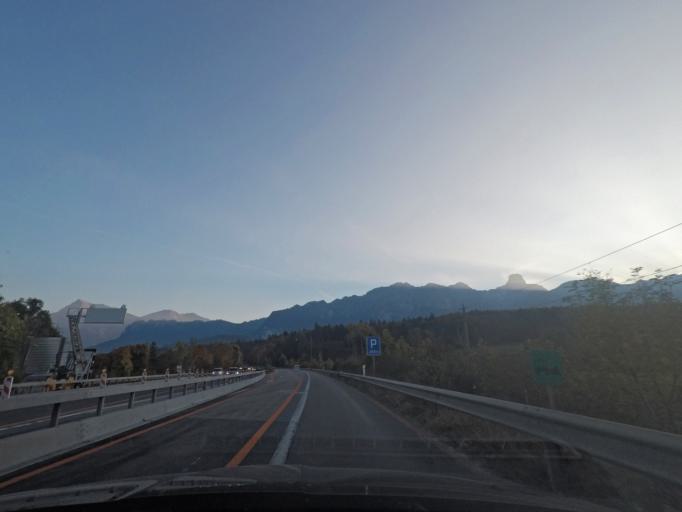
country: CH
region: Bern
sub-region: Thun District
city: Thun
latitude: 46.7383
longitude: 7.6010
